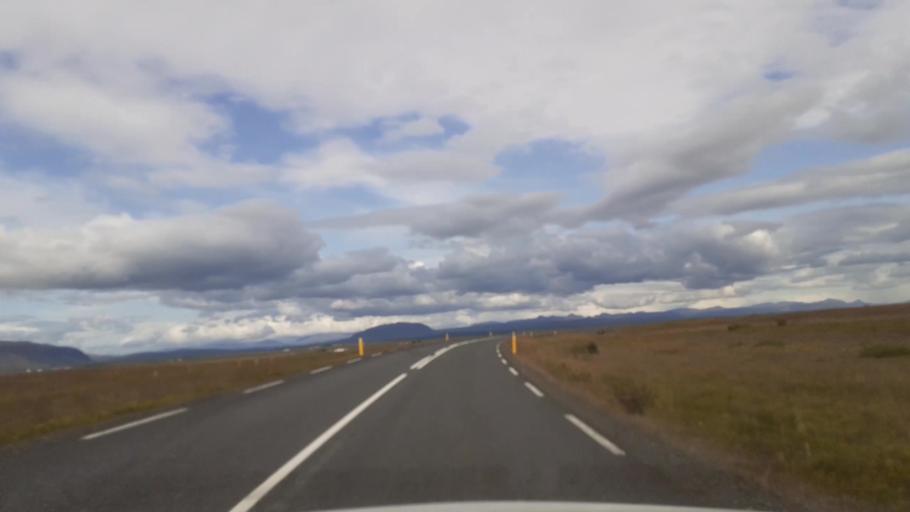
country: IS
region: South
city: Selfoss
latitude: 63.9227
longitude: -20.8519
